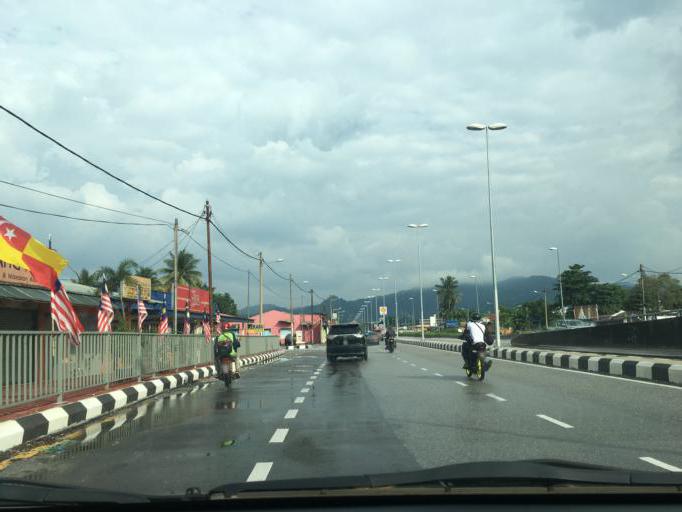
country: MY
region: Selangor
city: Rawang
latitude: 3.3148
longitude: 101.5785
